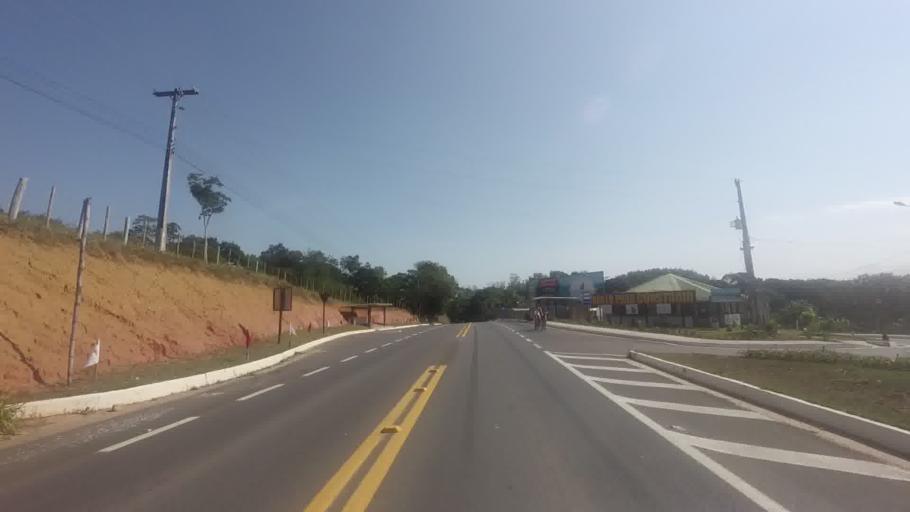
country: BR
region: Espirito Santo
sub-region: Piuma
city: Piuma
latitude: -20.8157
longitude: -40.6887
